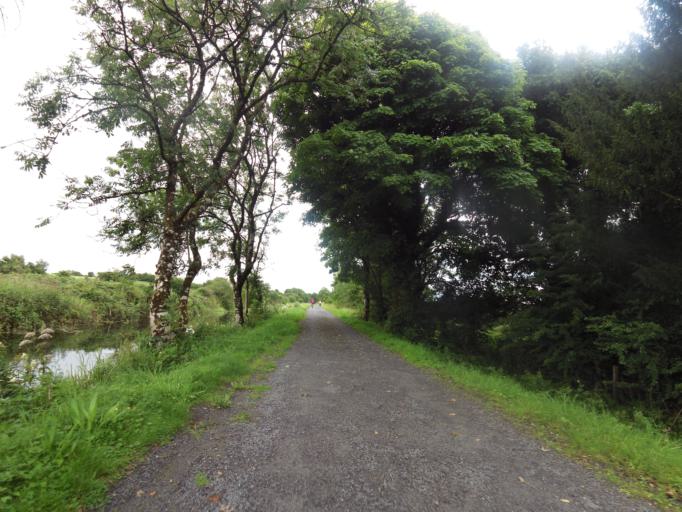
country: IE
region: Leinster
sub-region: An Iarmhi
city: An Muileann gCearr
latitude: 53.5150
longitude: -7.4294
